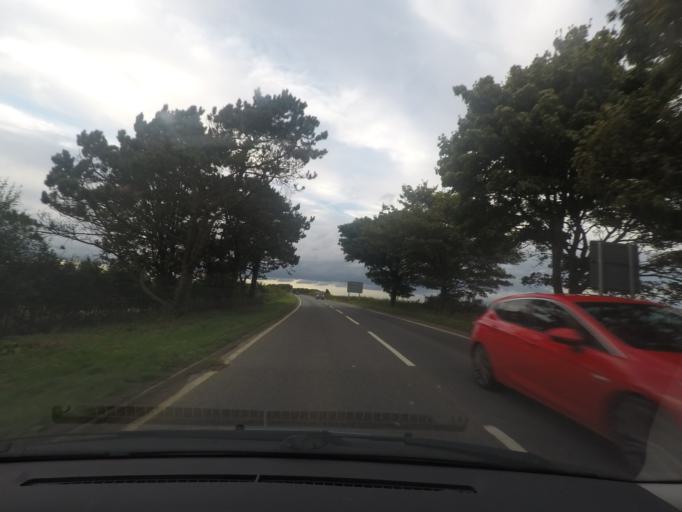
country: GB
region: England
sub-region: Lincolnshire
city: Alford
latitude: 53.2424
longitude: 0.1138
